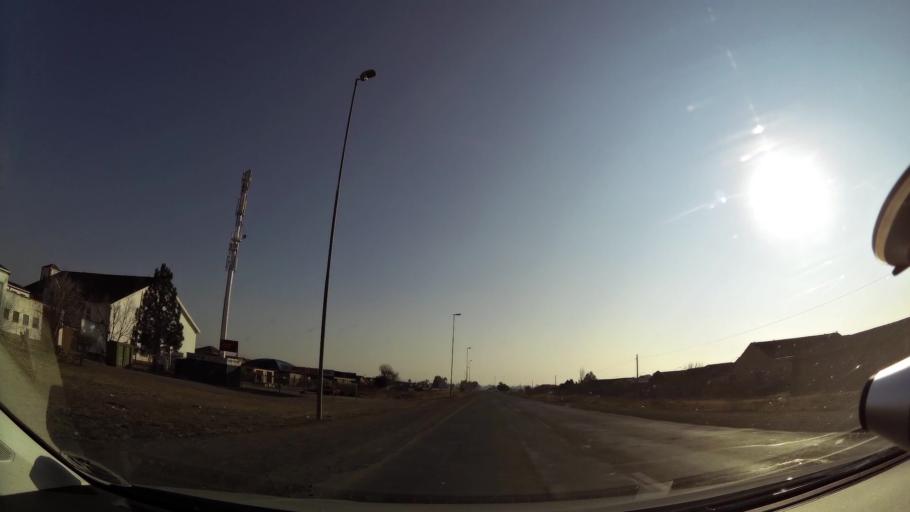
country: ZA
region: Orange Free State
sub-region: Mangaung Metropolitan Municipality
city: Bloemfontein
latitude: -29.1513
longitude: 26.2653
